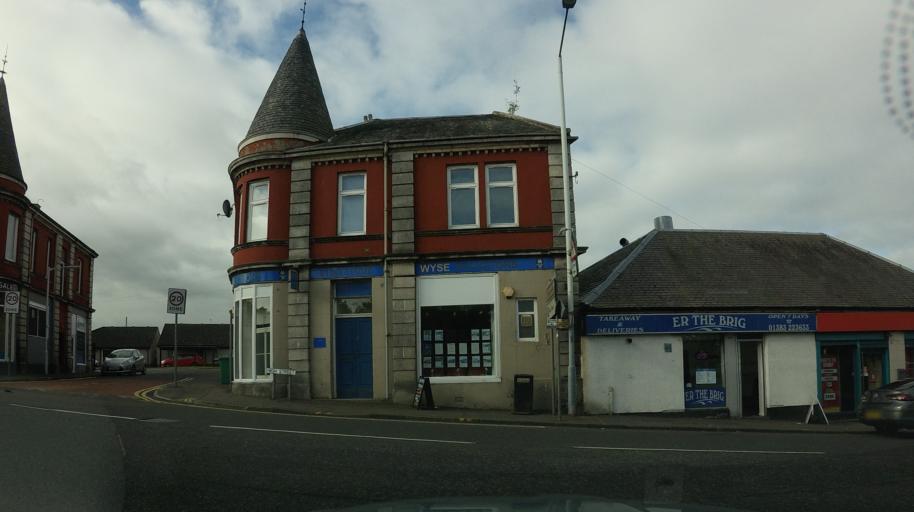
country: GB
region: Scotland
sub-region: Fife
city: Cowdenbeath
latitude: 56.1078
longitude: -3.3420
